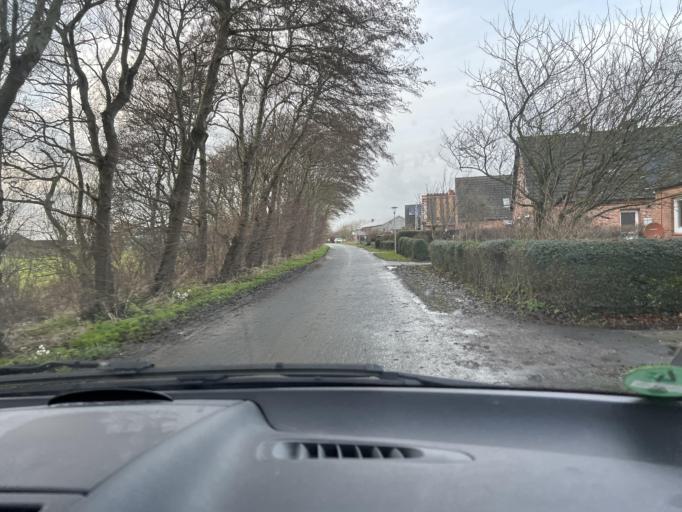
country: DE
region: Schleswig-Holstein
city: Hedwigenkoog
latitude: 54.1774
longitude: 8.8192
